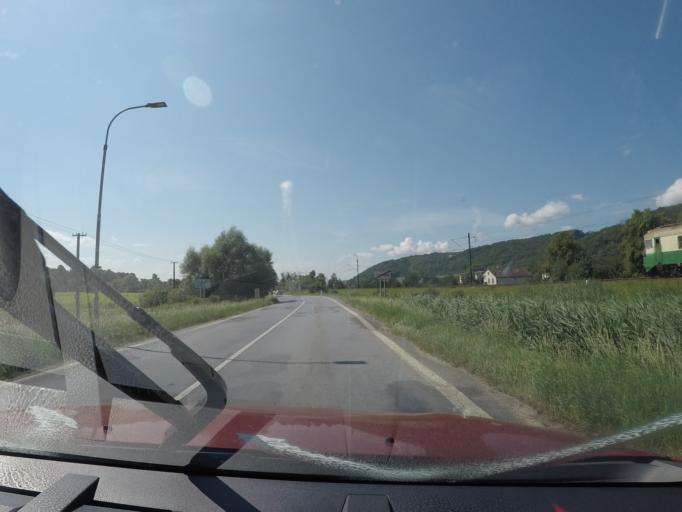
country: SK
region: Presovsky
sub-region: Okres Presov
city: Presov
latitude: 48.9559
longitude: 21.2415
